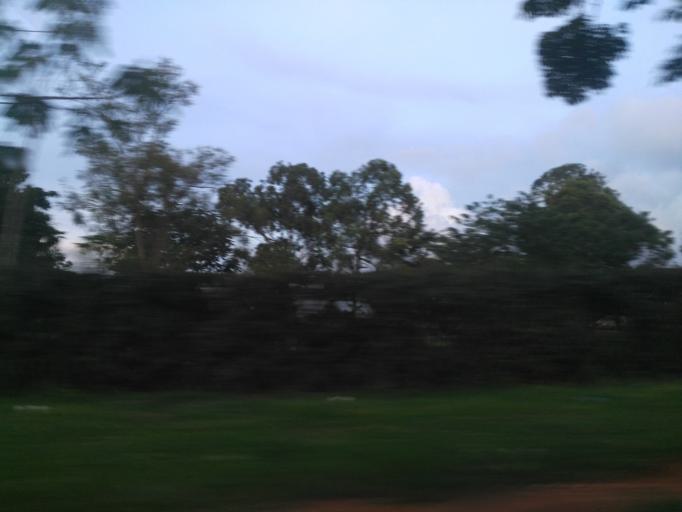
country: UG
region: Eastern Region
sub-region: Jinja District
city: Jinja
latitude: 0.4270
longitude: 33.2007
